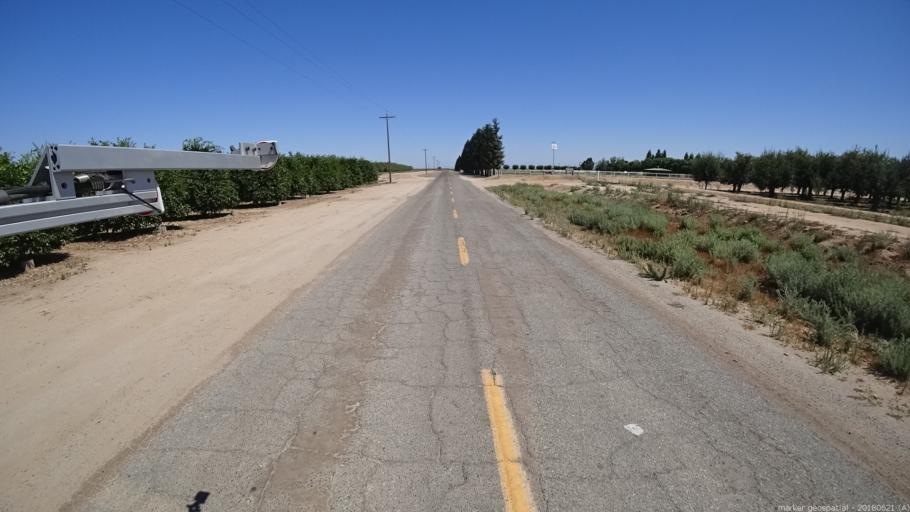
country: US
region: California
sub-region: Fresno County
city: Biola
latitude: 36.8617
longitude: -119.9294
